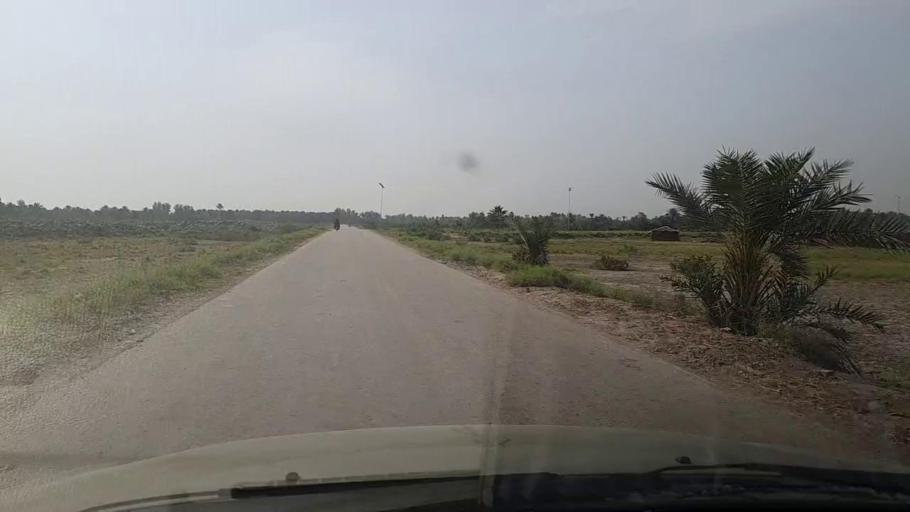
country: PK
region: Sindh
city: Gambat
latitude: 27.4600
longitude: 68.4824
